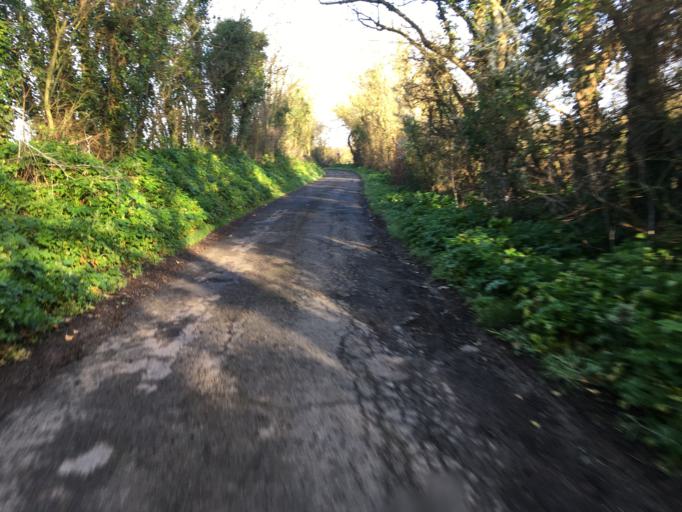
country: FR
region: Poitou-Charentes
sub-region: Departement de la Charente-Maritime
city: Nieul-sur-Mer
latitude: 46.1963
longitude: -1.1756
